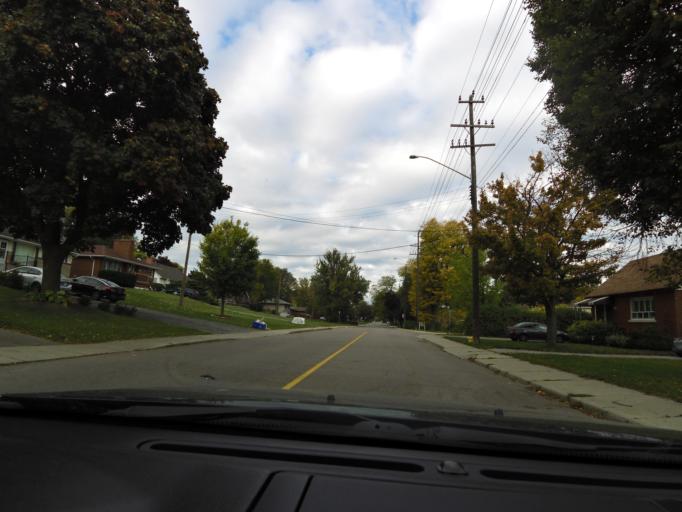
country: CA
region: Ontario
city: Hamilton
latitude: 43.2356
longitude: -79.9088
